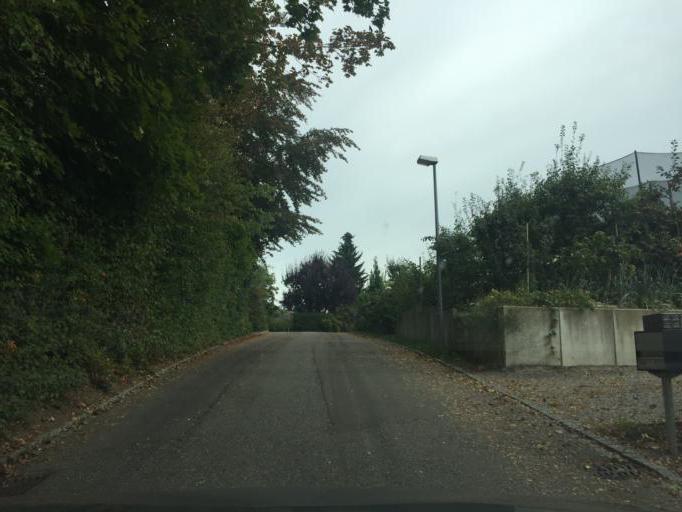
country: CH
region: Thurgau
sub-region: Frauenfeld District
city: Diessenhofen
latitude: 47.6882
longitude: 8.7394
